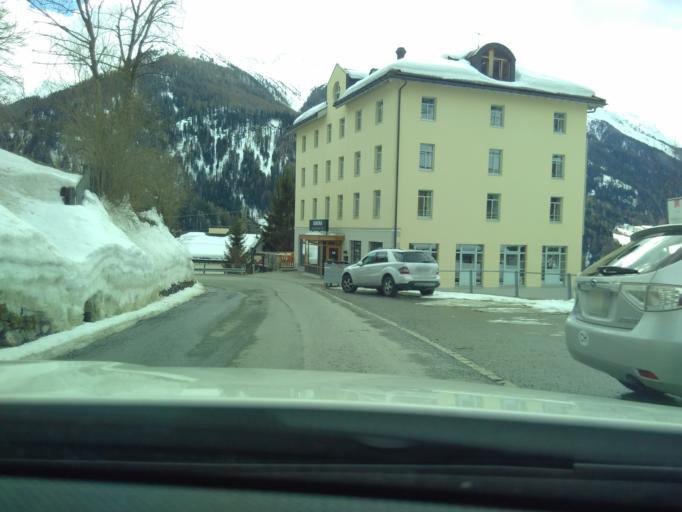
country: CH
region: Grisons
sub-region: Inn District
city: Scuol
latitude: 46.7744
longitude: 10.2033
